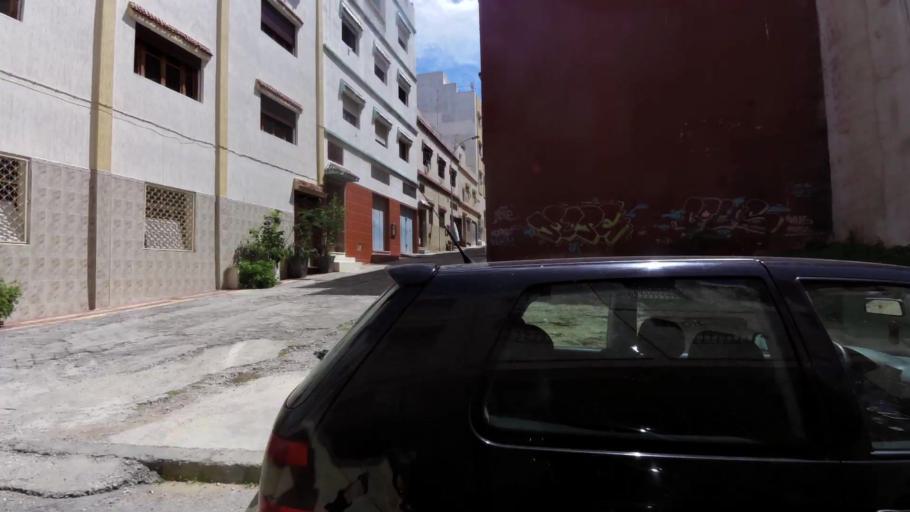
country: MA
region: Tanger-Tetouan
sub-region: Tanger-Assilah
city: Tangier
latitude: 35.7537
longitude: -5.8293
